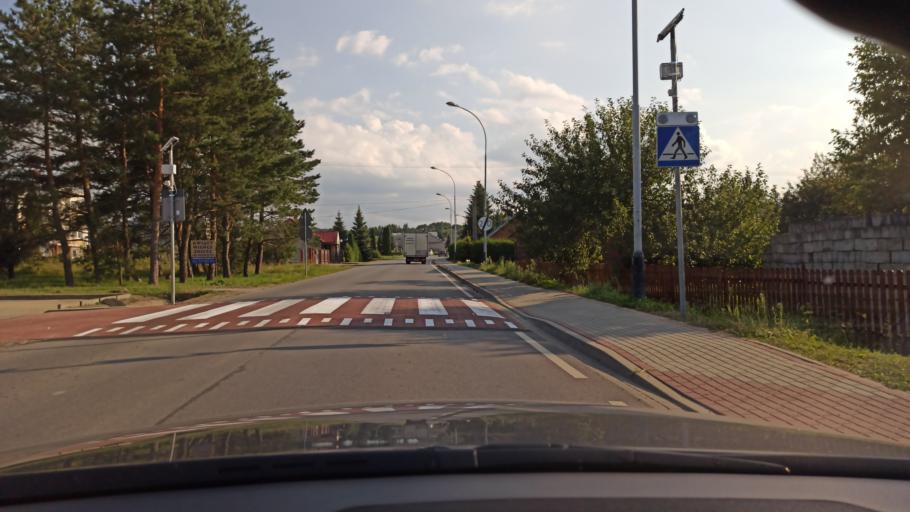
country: PL
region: Subcarpathian Voivodeship
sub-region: Powiat krosnienski
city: Miejsce Piastowe
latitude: 49.5999
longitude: 21.8018
